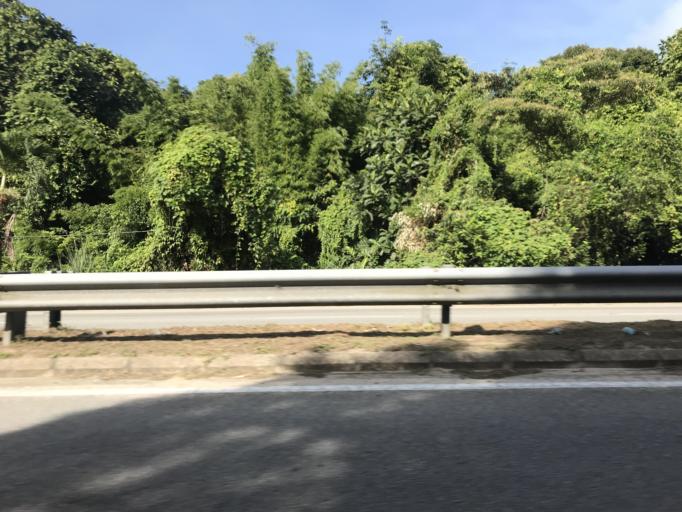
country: MY
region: Kelantan
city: Pasir Mas
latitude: 6.0620
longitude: 102.2075
